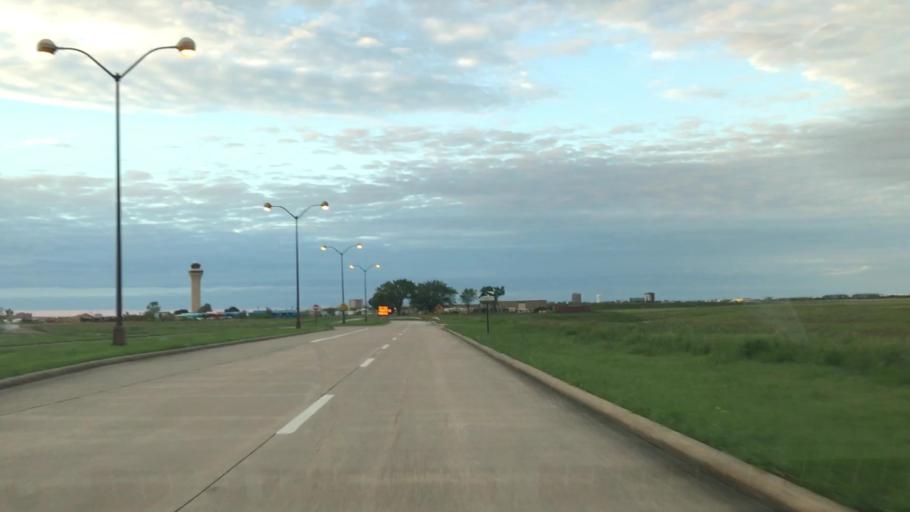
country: US
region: Texas
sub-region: Dallas County
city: Coppell
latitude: 32.8866
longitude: -97.0156
